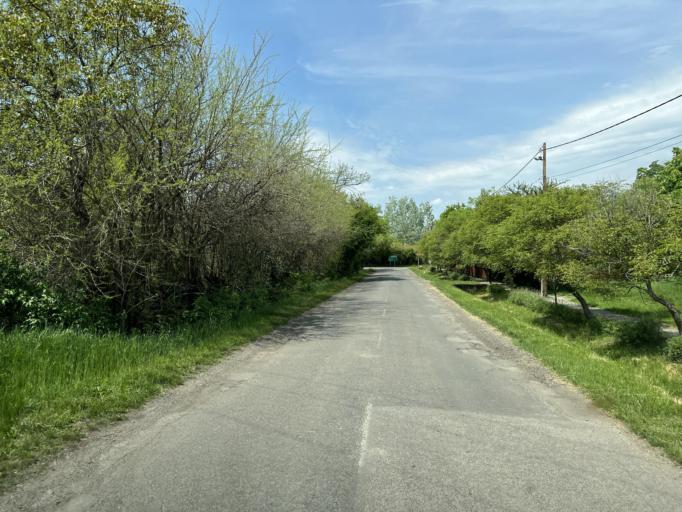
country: HU
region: Pest
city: Tapiogyorgye
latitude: 47.3305
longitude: 19.9535
